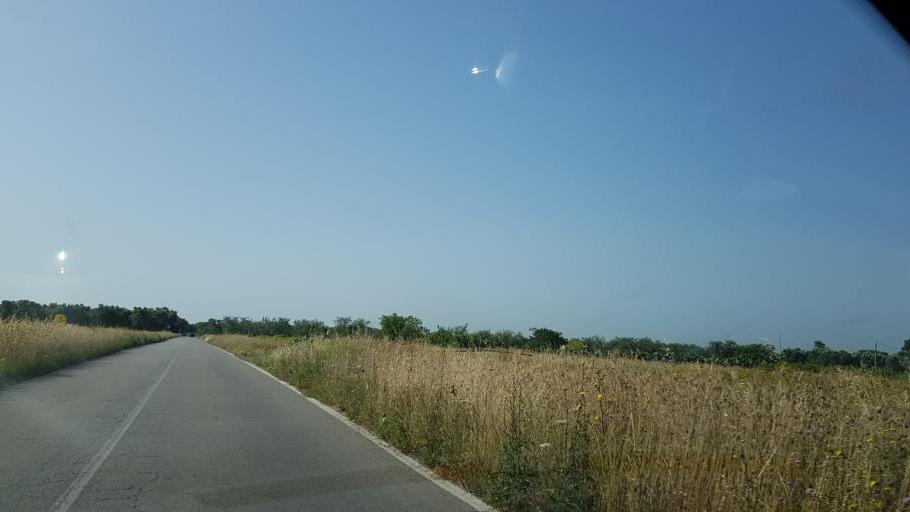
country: IT
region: Apulia
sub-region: Provincia di Brindisi
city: Mesagne
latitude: 40.5219
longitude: 17.8217
